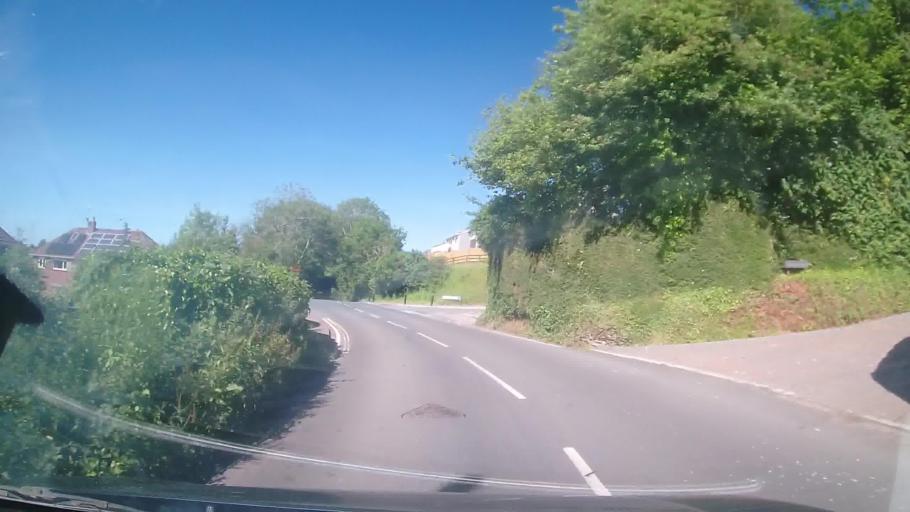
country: GB
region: England
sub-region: Borough of Torbay
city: Brixham
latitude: 50.3790
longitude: -3.5330
